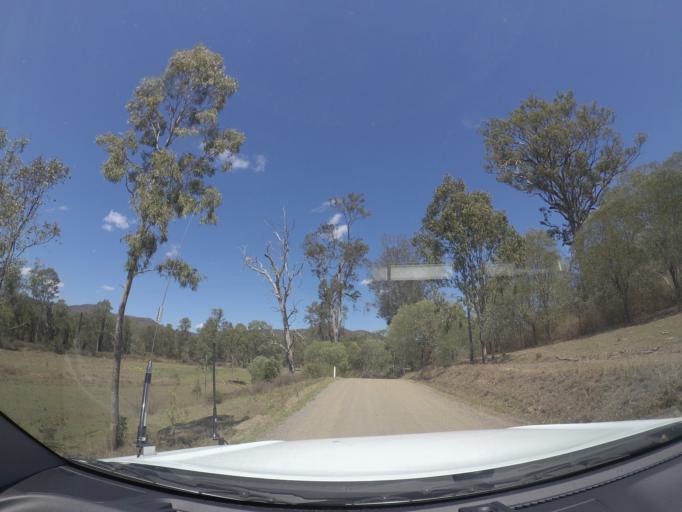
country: AU
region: Queensland
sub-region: Logan
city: Cedar Vale
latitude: -27.8648
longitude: 152.8523
